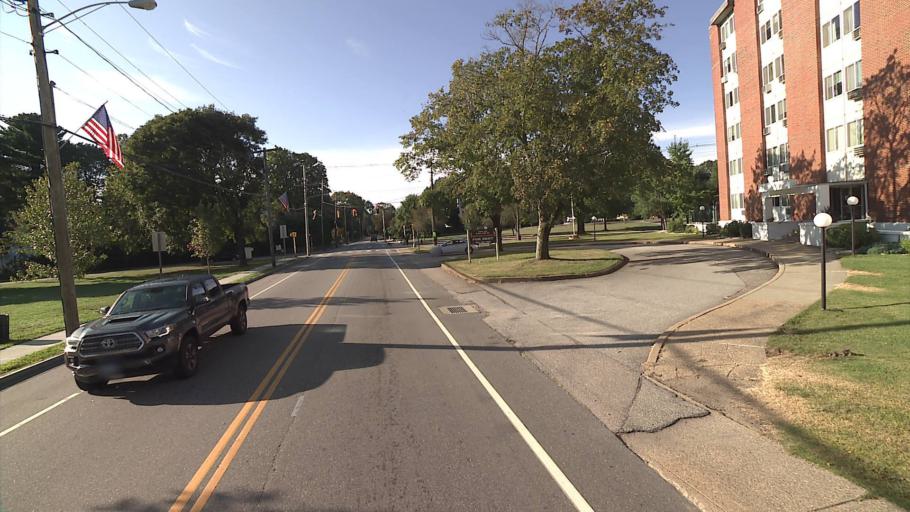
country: US
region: Connecticut
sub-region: New London County
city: Norwich
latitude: 41.5356
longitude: -72.0835
